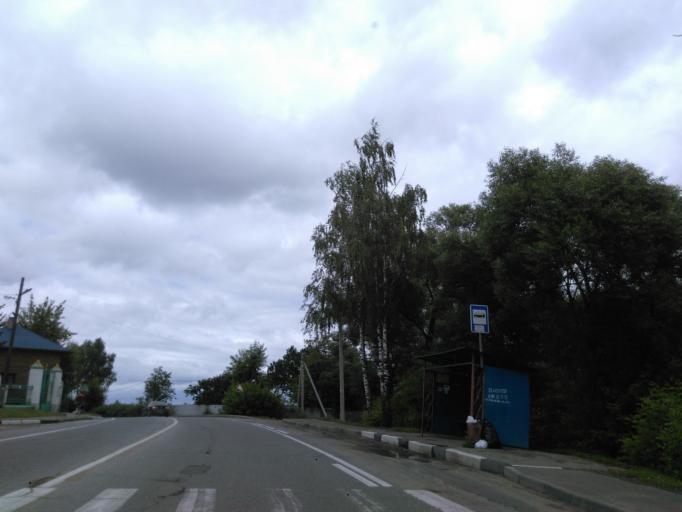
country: RU
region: Moskovskaya
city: Solnechnogorsk
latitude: 56.1475
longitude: 36.9174
